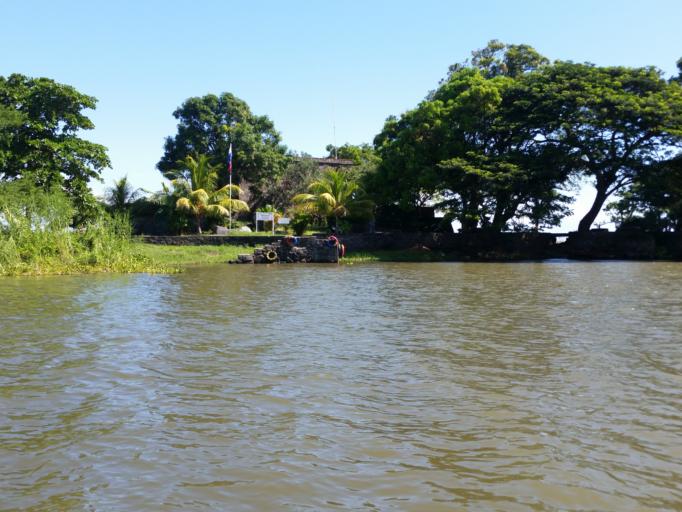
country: NI
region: Granada
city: Granada
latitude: 11.9208
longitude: -85.9193
